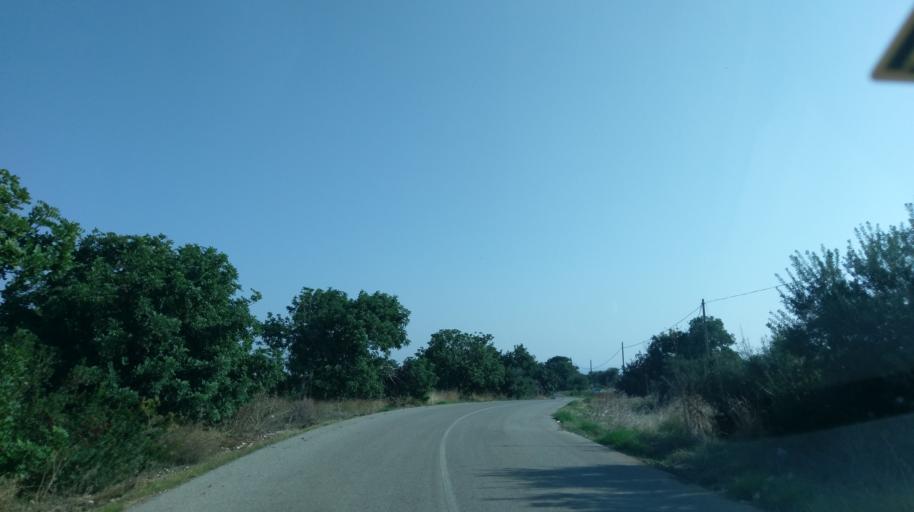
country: CY
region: Ammochostos
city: Leonarisso
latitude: 35.4704
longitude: 34.2094
